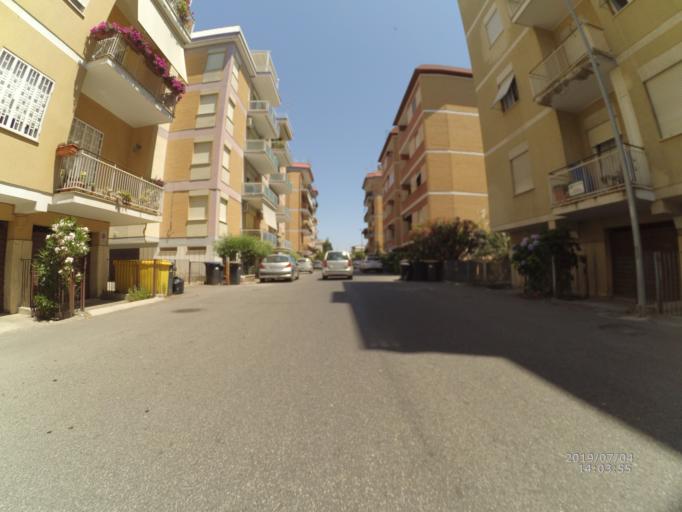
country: IT
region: Latium
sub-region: Provincia di Latina
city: Terracina
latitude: 41.2860
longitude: 13.2428
